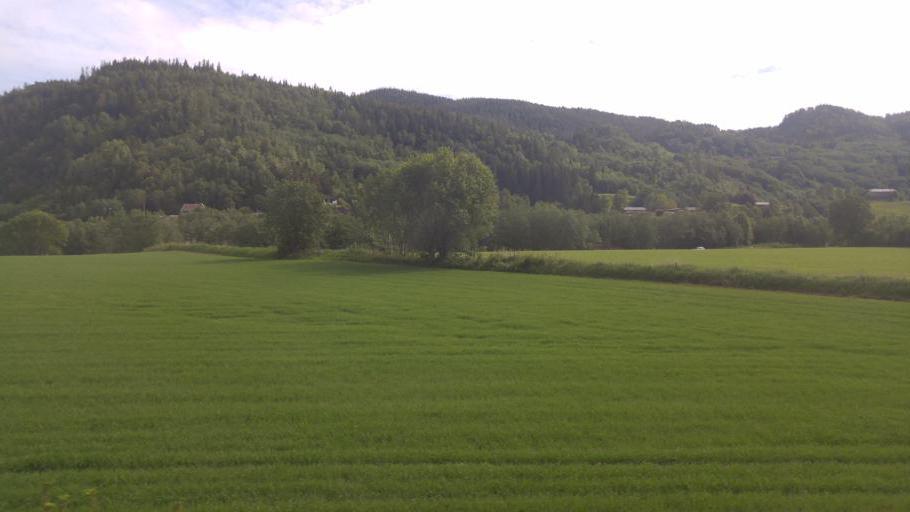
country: NO
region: Sor-Trondelag
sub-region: Midtre Gauldal
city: Storen
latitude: 63.0923
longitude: 10.2375
